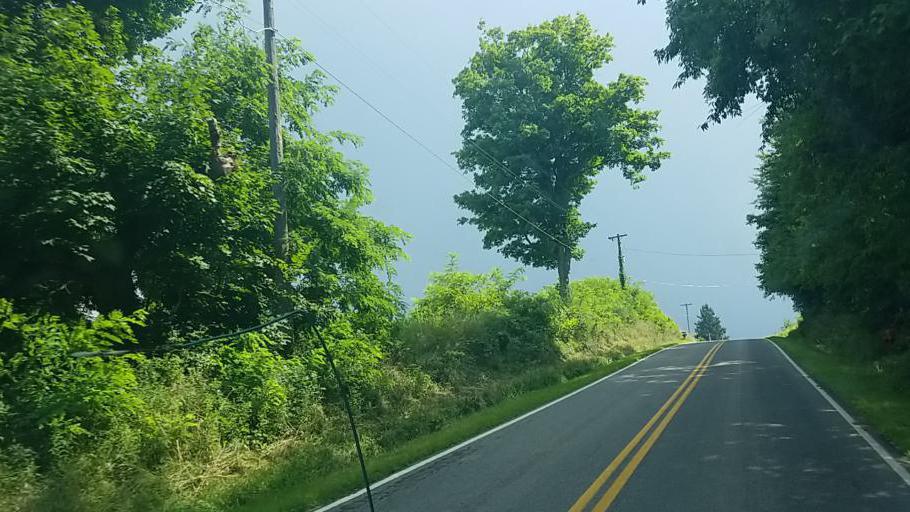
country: US
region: Ohio
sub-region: Medina County
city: Lodi
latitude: 41.0601
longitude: -82.0054
